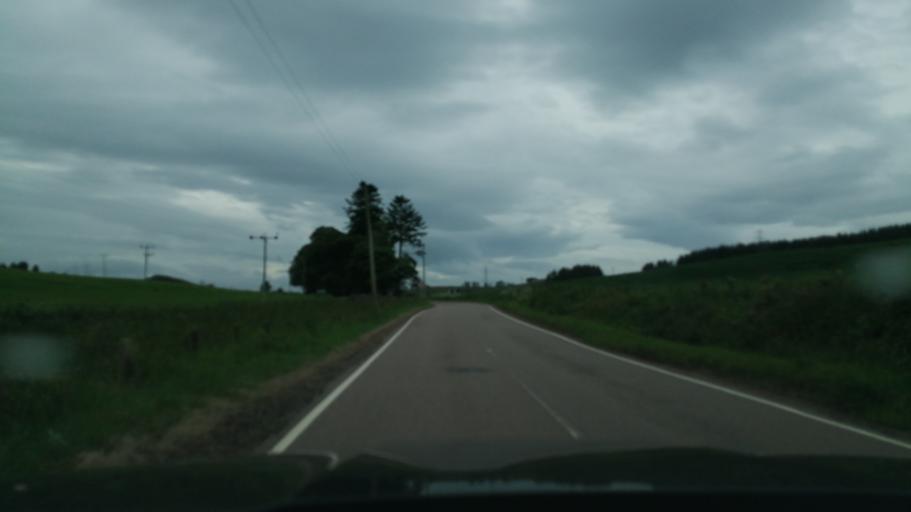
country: GB
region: Scotland
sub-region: Moray
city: Cullen
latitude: 57.6092
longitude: -2.8517
